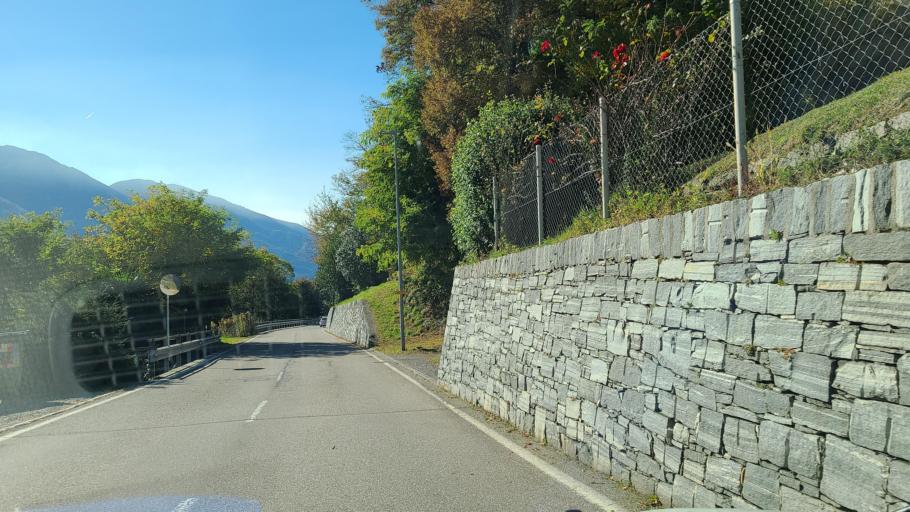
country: CH
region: Ticino
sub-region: Locarno District
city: Gordola
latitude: 46.1849
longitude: 8.8423
